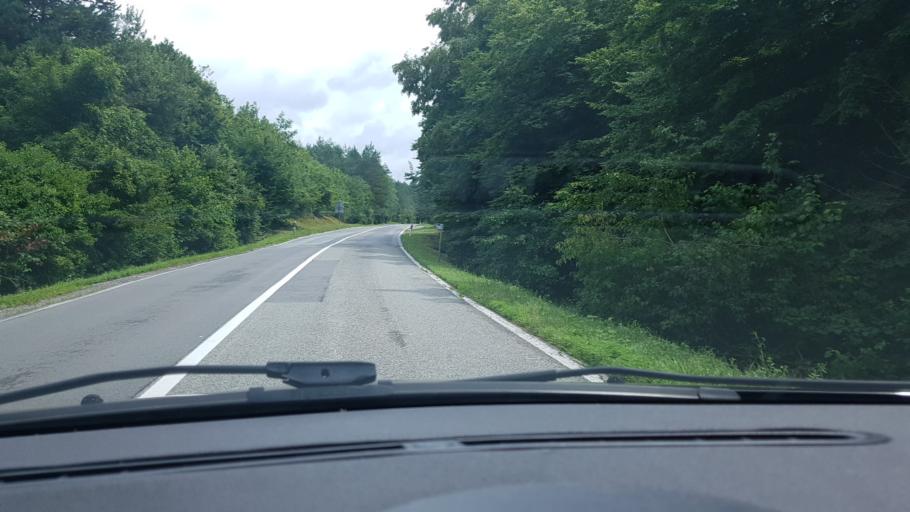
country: HR
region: Licko-Senjska
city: Jezerce
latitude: 44.9390
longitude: 15.6814
